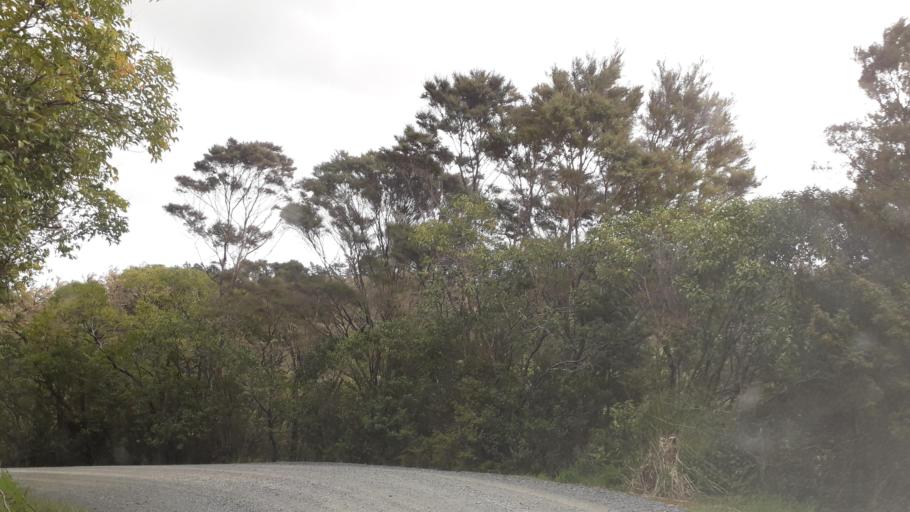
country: NZ
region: Northland
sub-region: Far North District
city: Waimate North
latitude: -35.3042
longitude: 173.5634
